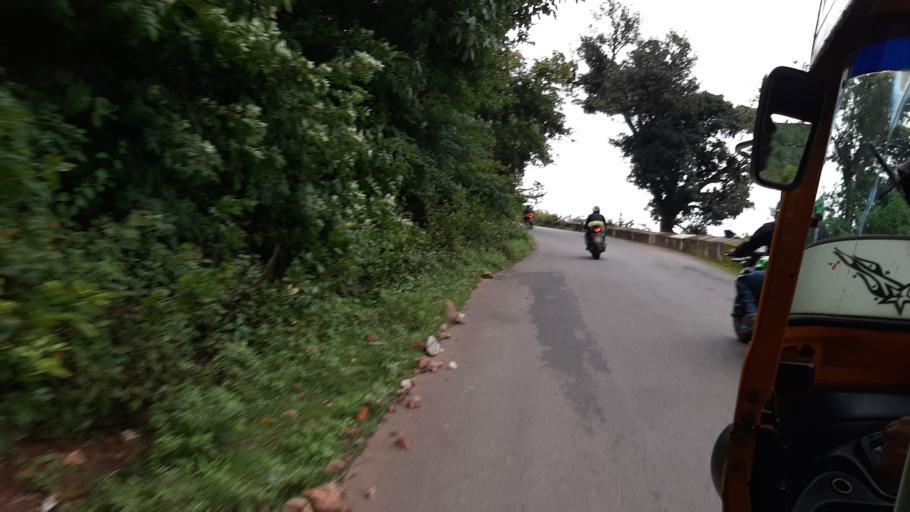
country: IN
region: Andhra Pradesh
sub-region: Vizianagaram District
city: Salur
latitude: 18.2421
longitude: 83.0272
